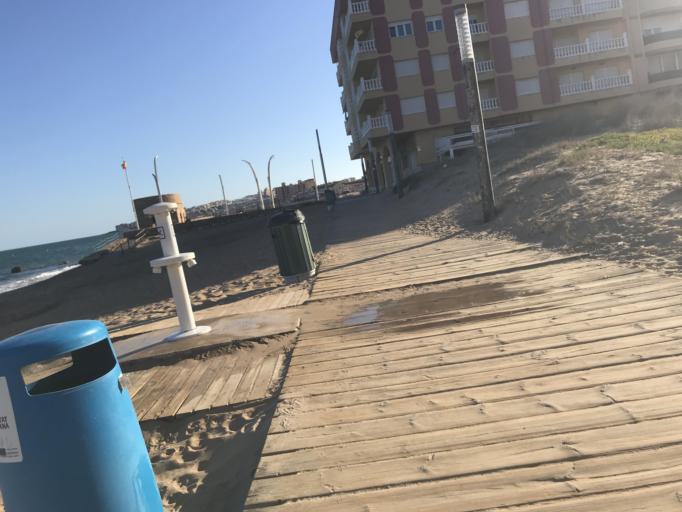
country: ES
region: Valencia
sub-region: Provincia de Alicante
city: Torrevieja
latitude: 38.0271
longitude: -0.6526
